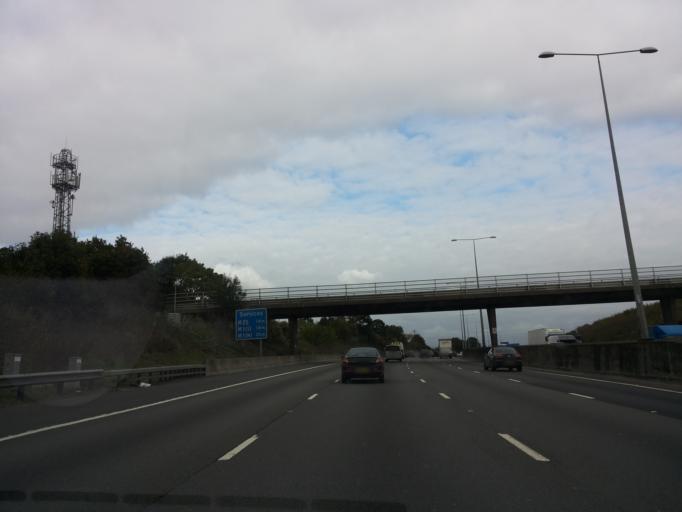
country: GB
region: England
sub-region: Hertfordshire
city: Chorleywood
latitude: 51.6697
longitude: -0.4893
